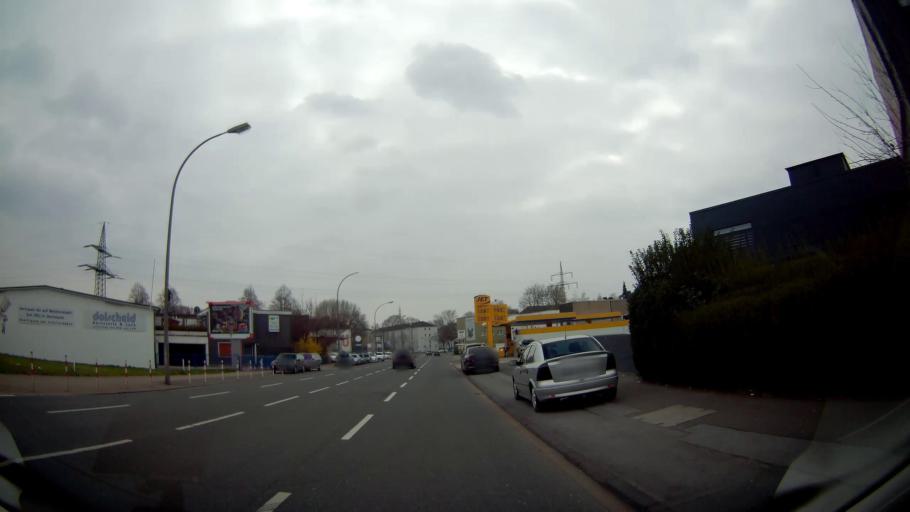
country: DE
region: North Rhine-Westphalia
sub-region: Regierungsbezirk Arnsberg
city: Dortmund
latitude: 51.5200
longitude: 7.4886
